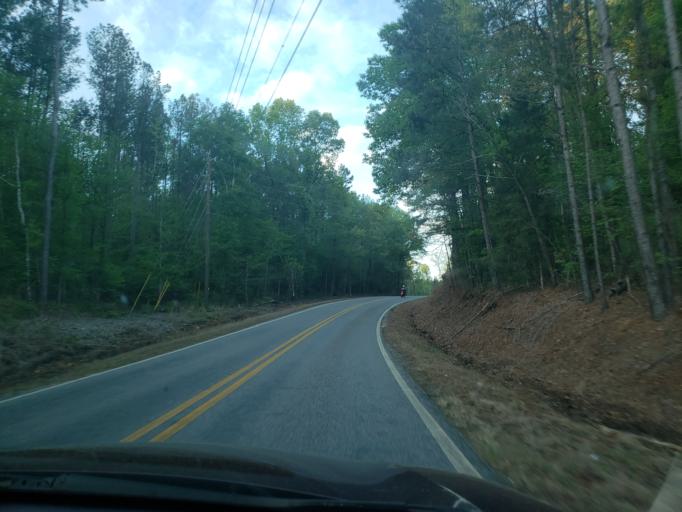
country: US
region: Alabama
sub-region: Elmore County
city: Tallassee
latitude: 32.6737
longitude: -85.8834
